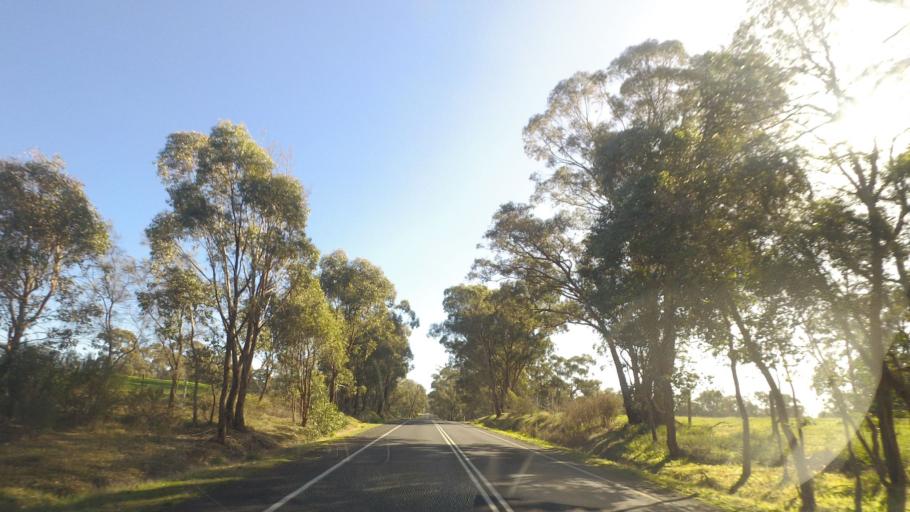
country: AU
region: Victoria
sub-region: Greater Bendigo
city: Kennington
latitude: -36.9204
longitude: 144.3417
